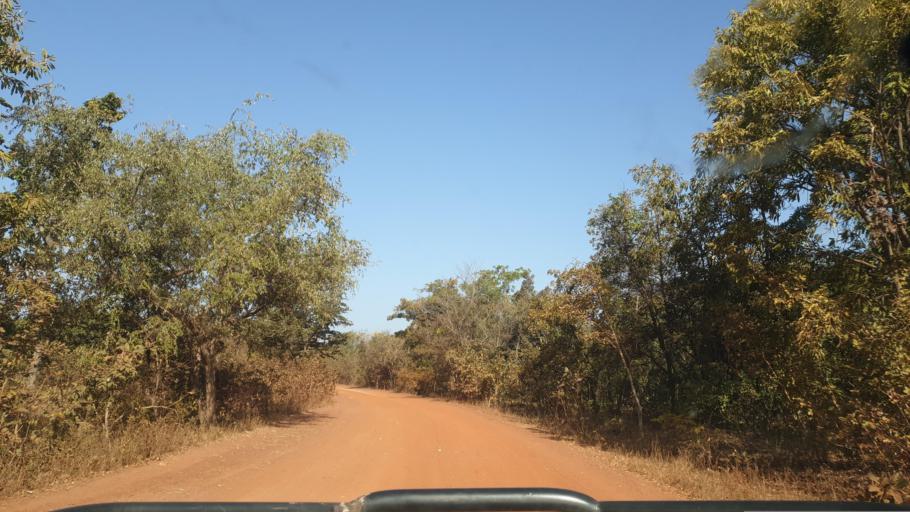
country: ML
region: Sikasso
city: Bougouni
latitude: 11.7837
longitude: -6.9088
